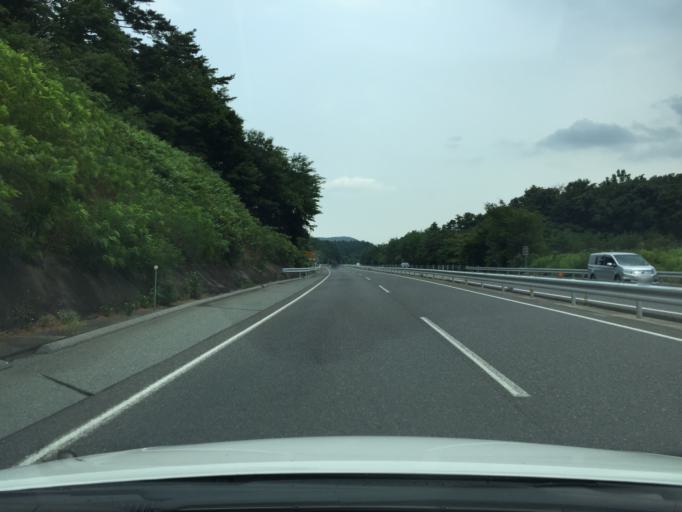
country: JP
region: Fukushima
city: Iwaki
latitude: 37.0666
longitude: 140.7935
